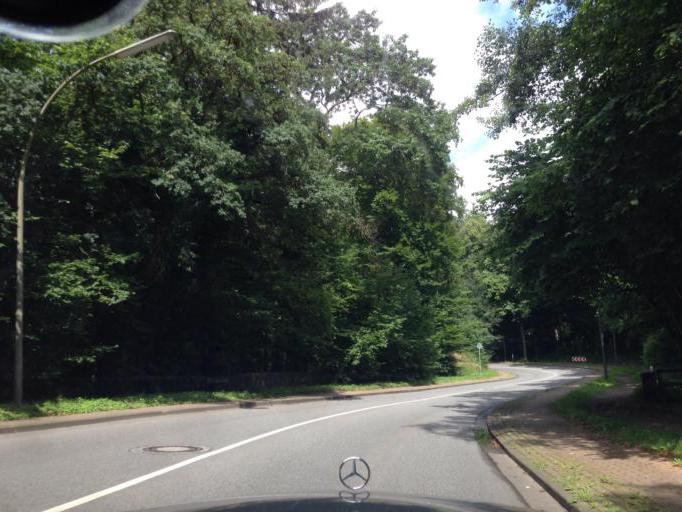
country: DE
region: Hamburg
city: Wohldorf-Ohlstedt
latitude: 53.6867
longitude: 10.1304
